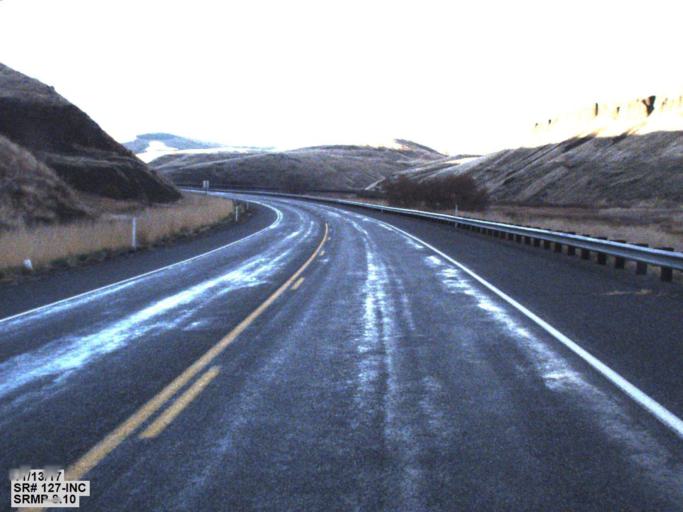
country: US
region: Washington
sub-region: Garfield County
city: Pomeroy
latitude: 46.6029
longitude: -117.7844
